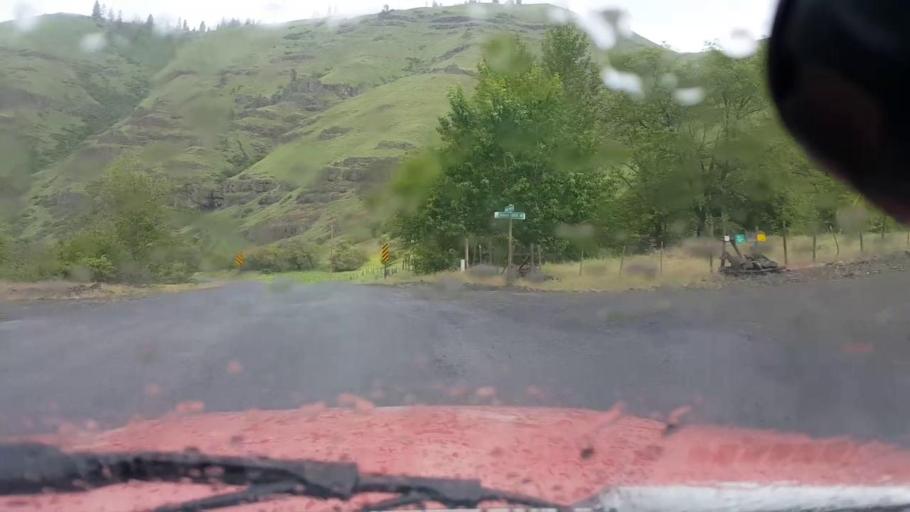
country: US
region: Washington
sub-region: Asotin County
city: Asotin
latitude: 46.0326
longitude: -117.3187
